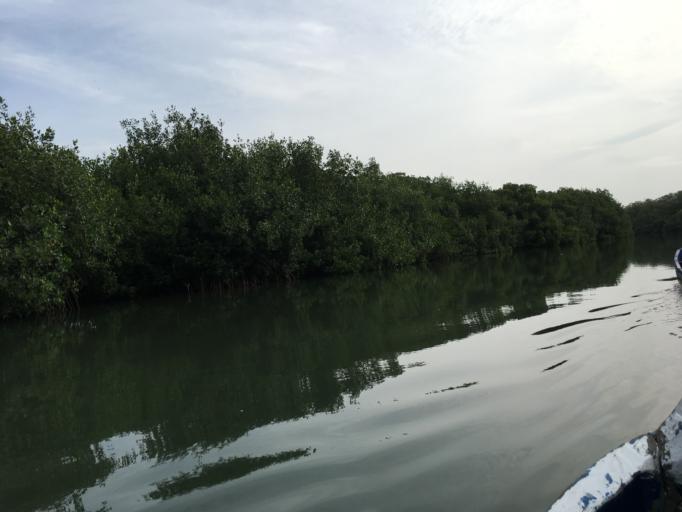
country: CO
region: Bolivar
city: Cartagena
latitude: 10.4892
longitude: -75.4882
